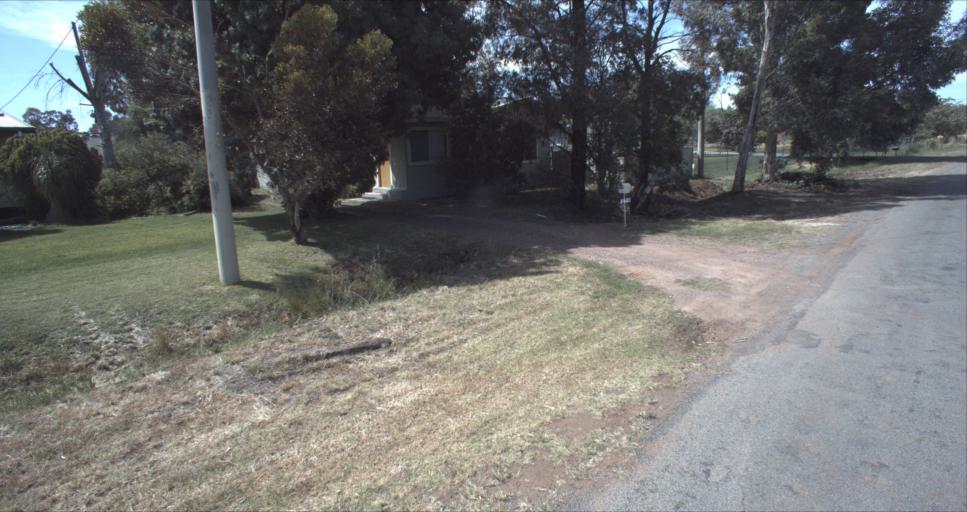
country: AU
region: New South Wales
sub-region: Leeton
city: Leeton
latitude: -34.5694
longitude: 146.4561
